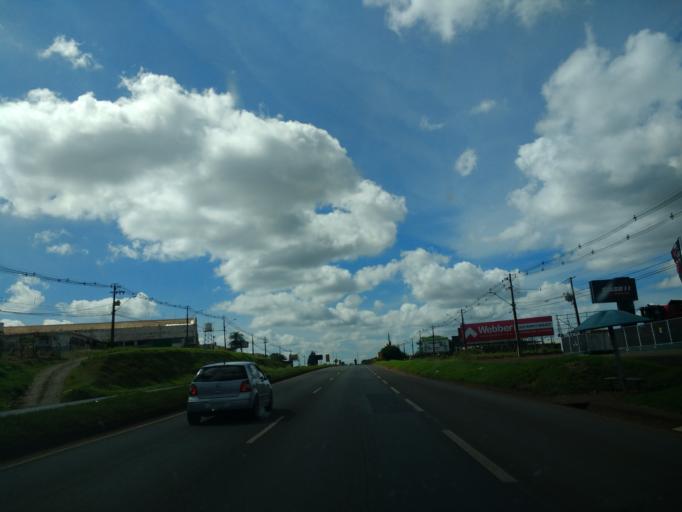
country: BR
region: Parana
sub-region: Maringa
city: Maringa
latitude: -23.4406
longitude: -51.9800
